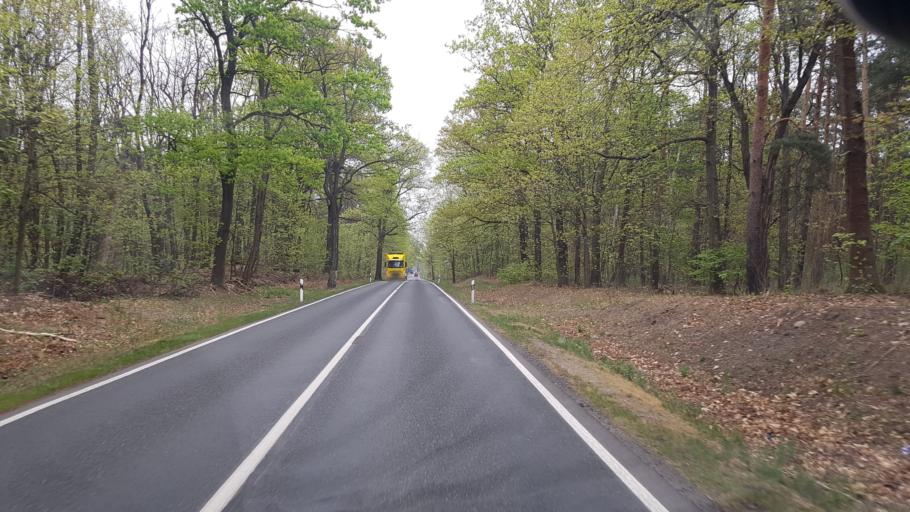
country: DE
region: Brandenburg
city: Altdobern
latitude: 51.6275
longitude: 14.0278
